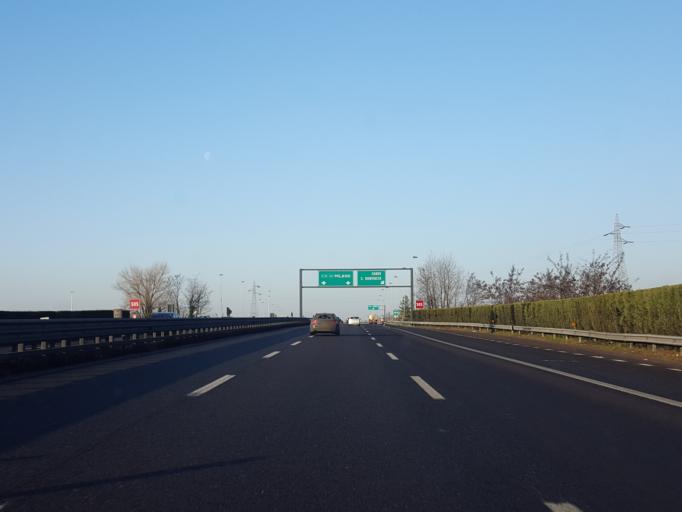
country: IT
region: Veneto
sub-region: Provincia di Verona
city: Soave
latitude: 45.4089
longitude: 11.2565
